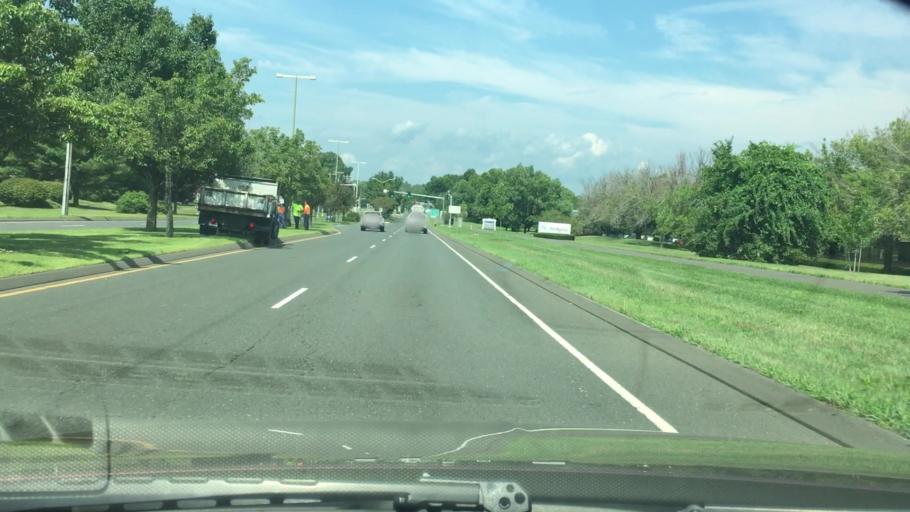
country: US
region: Connecticut
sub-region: Hartford County
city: Windsor
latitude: 41.8784
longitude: -72.7008
